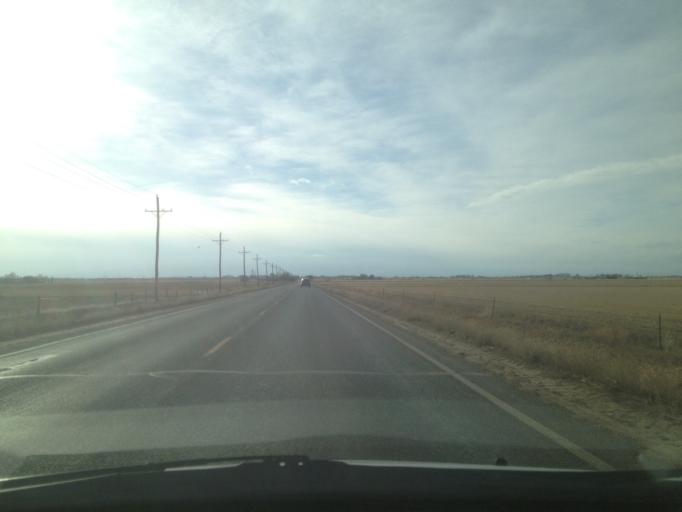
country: US
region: Colorado
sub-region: Weld County
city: Hudson
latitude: 40.0806
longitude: -104.6679
